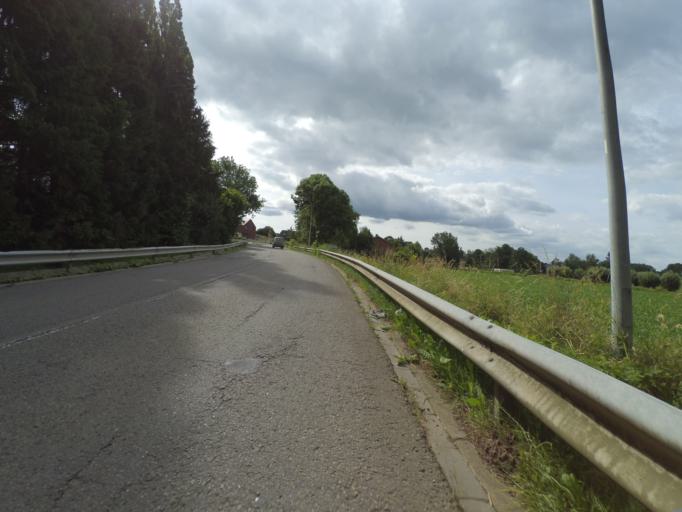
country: BE
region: Wallonia
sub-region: Province de Liege
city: Lontzen
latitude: 50.6869
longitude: 6.0344
